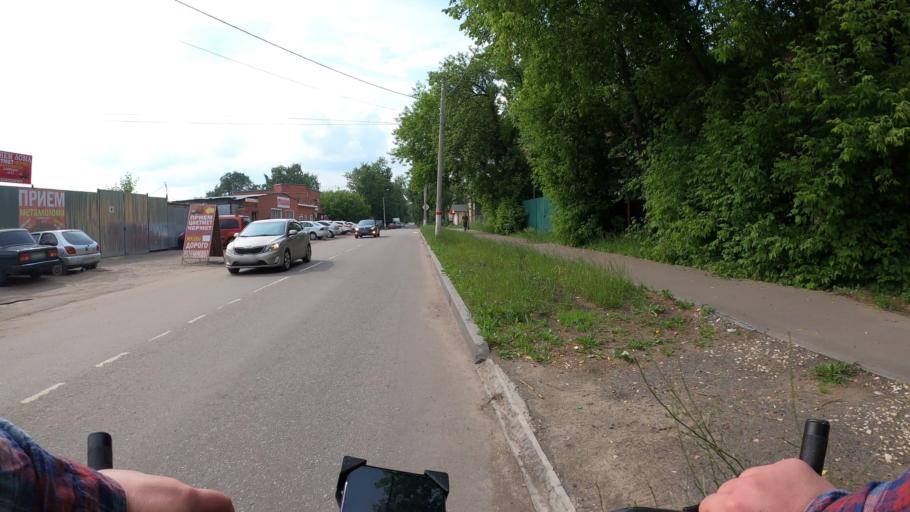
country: RU
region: Moskovskaya
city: Zhukovskiy
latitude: 55.6058
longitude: 38.1102
